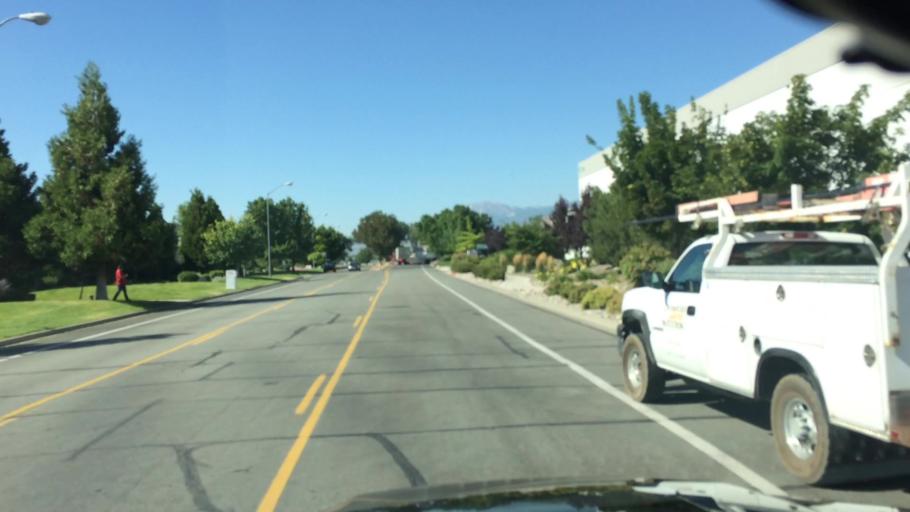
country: US
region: Nevada
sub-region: Washoe County
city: Sparks
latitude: 39.5022
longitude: -119.7545
